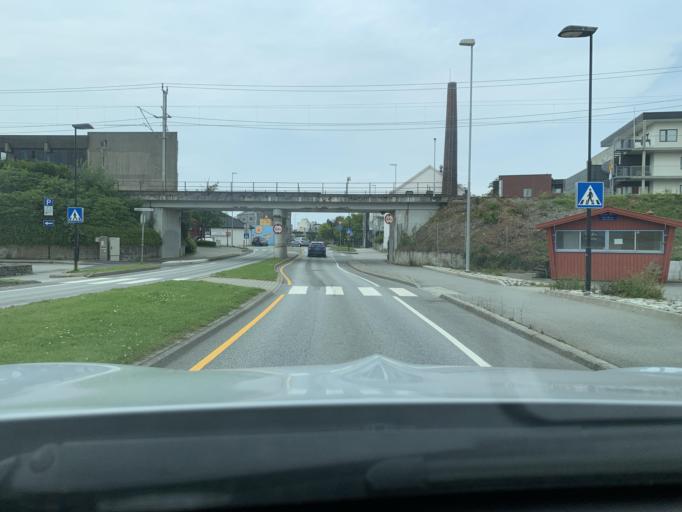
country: NO
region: Rogaland
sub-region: Time
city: Bryne
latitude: 58.7358
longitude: 5.6507
